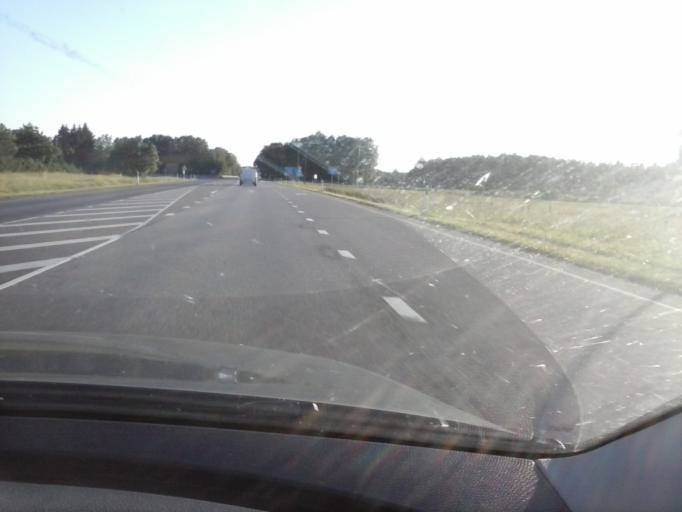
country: EE
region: Laeaene
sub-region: Ridala Parish
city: Uuemoisa
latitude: 58.9567
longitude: 23.7862
